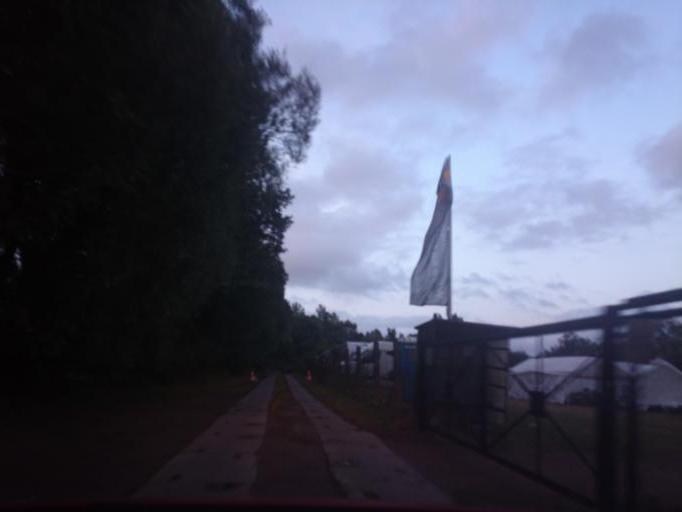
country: DE
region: Mecklenburg-Vorpommern
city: Barth
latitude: 54.3654
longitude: 12.7550
